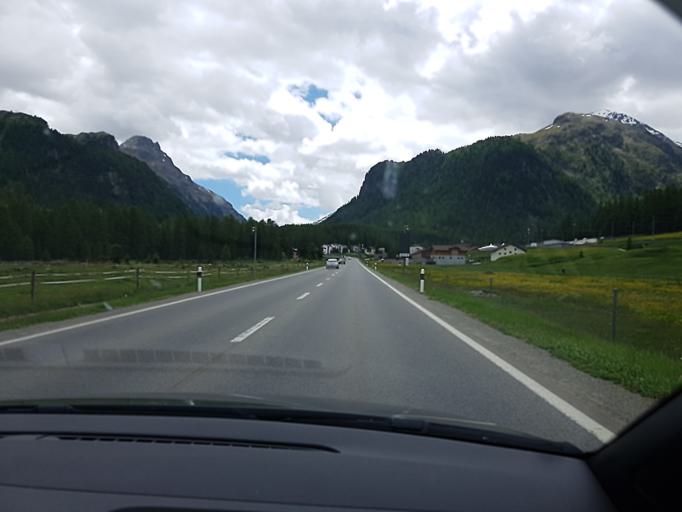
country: CH
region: Grisons
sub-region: Maloja District
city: Pontresina
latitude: 46.4957
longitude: 9.8931
